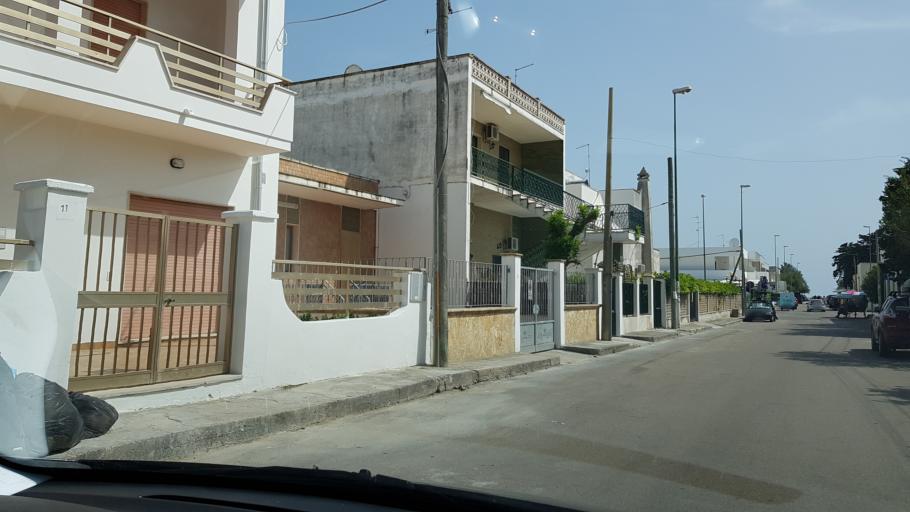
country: IT
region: Apulia
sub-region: Provincia di Lecce
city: Porto Cesareo
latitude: 40.2882
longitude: 17.8520
